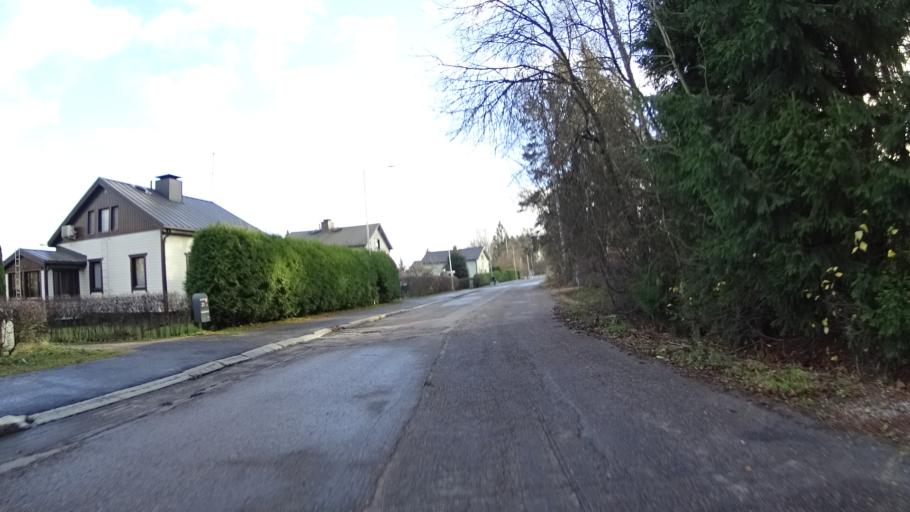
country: FI
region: Uusimaa
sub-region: Helsinki
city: Vantaa
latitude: 60.3051
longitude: 25.0299
